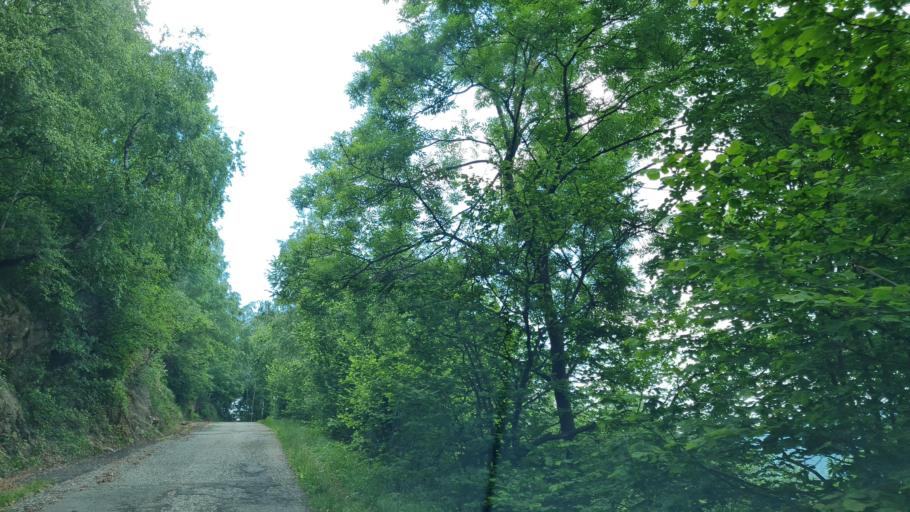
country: IT
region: Piedmont
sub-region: Provincia di Biella
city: Sordevolo
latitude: 45.5950
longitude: 7.9509
